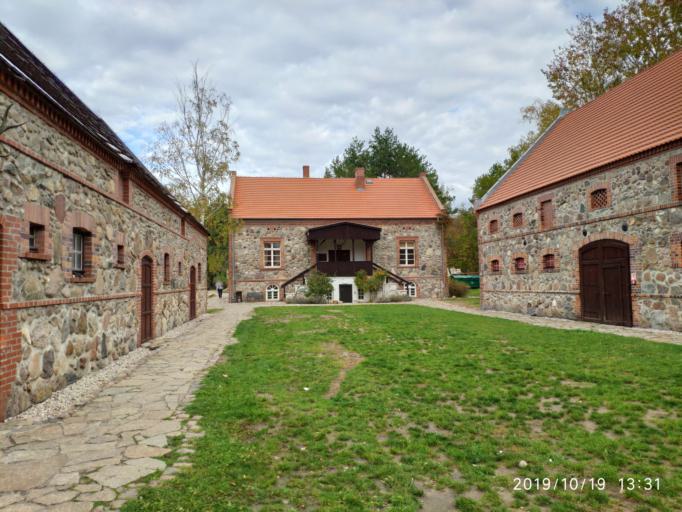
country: PL
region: Lubusz
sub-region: Powiat zielonogorski
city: Ochla
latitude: 51.8897
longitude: 15.4771
